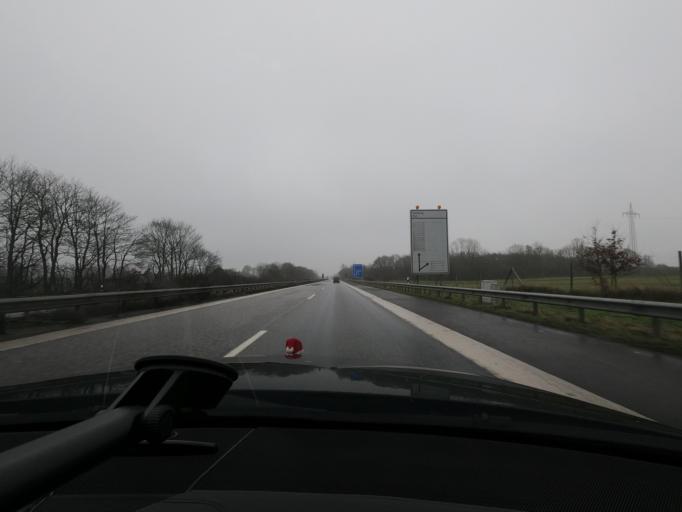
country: DE
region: Schleswig-Holstein
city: Neu Duvenstedt
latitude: 54.3534
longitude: 9.6882
